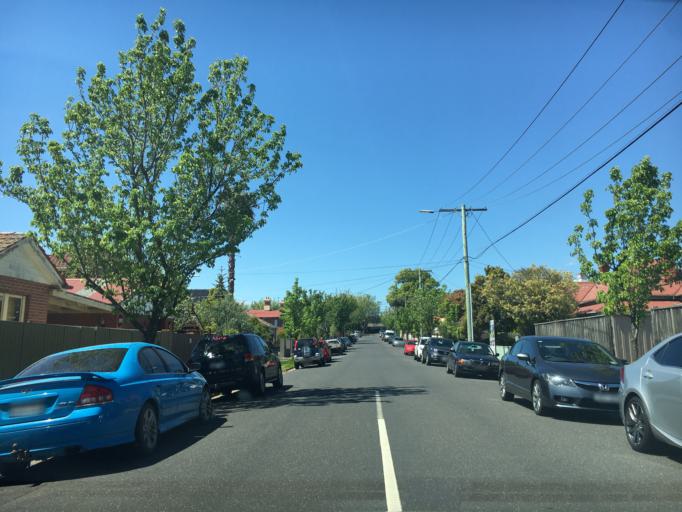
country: AU
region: Victoria
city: Hughesdale
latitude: -37.8956
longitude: 145.0906
